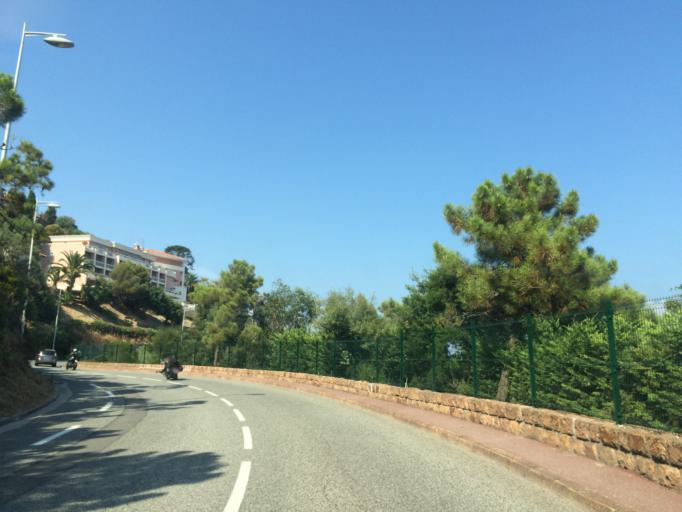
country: FR
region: Provence-Alpes-Cote d'Azur
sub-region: Departement des Alpes-Maritimes
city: Theoule-sur-Mer
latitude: 43.4990
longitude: 6.9511
